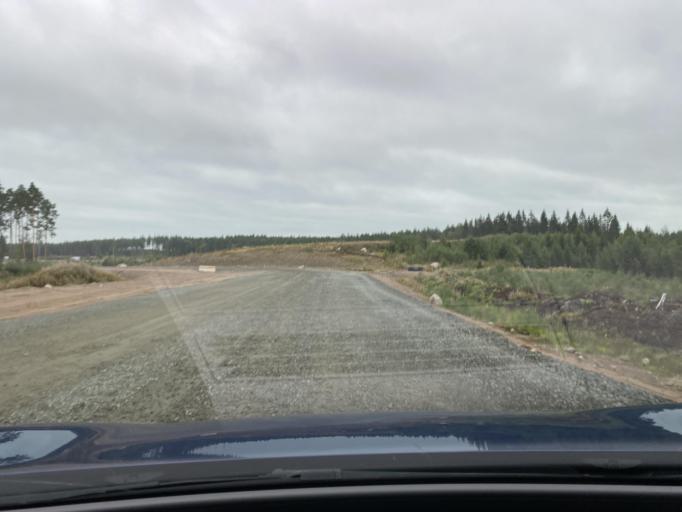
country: FI
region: Kymenlaakso
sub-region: Kouvola
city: Iitti
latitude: 60.8765
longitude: 26.4926
